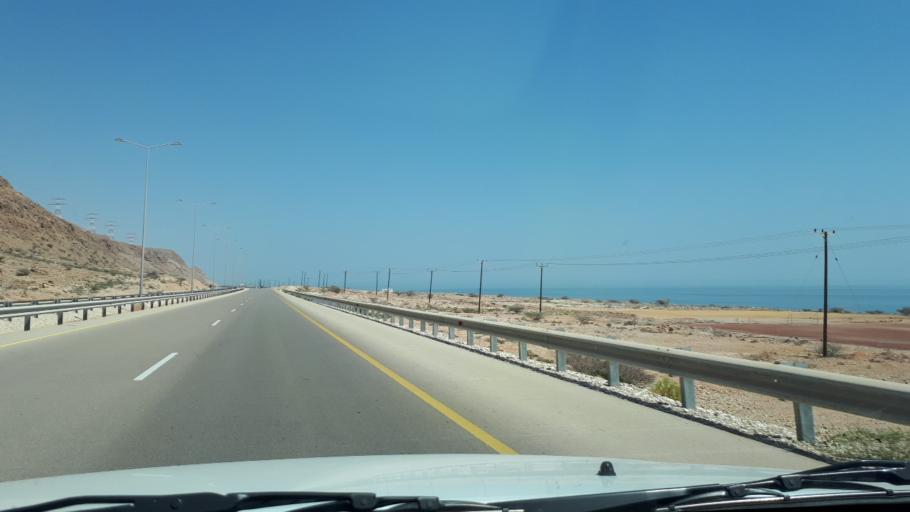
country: OM
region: Ash Sharqiyah
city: Sur
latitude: 22.7954
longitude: 59.2727
